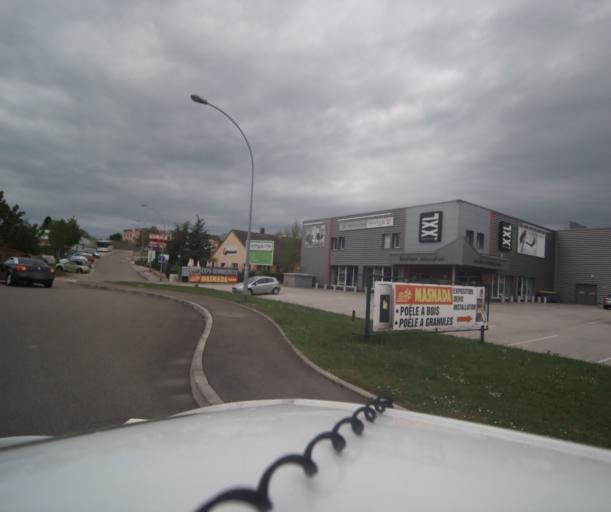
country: FR
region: Franche-Comte
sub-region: Departement du Doubs
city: Franois
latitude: 47.2163
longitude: 5.9444
